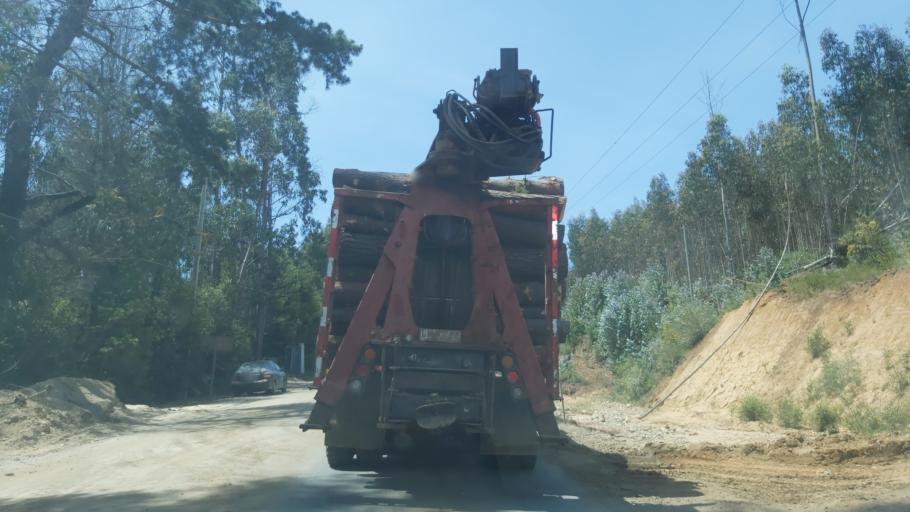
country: CL
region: Maule
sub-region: Provincia de Talca
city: Constitucion
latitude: -35.4447
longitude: -72.4650
